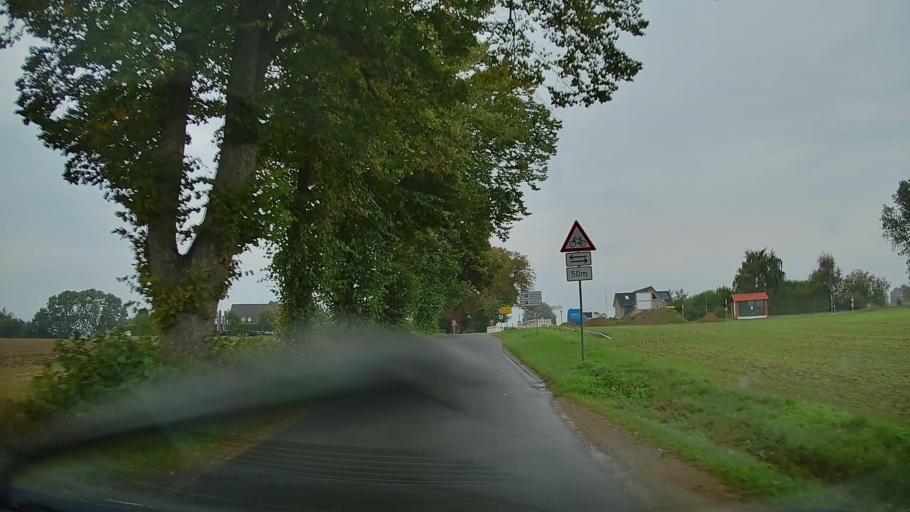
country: DE
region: Mecklenburg-Vorpommern
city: Kalkhorst
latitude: 53.9811
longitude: 11.0063
